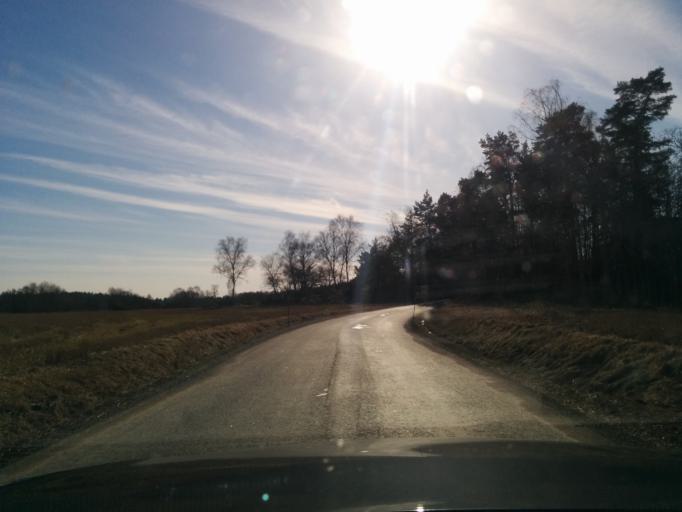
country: SE
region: Stockholm
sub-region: Vallentuna Kommun
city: Vallentuna
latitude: 59.5169
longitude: 18.0142
